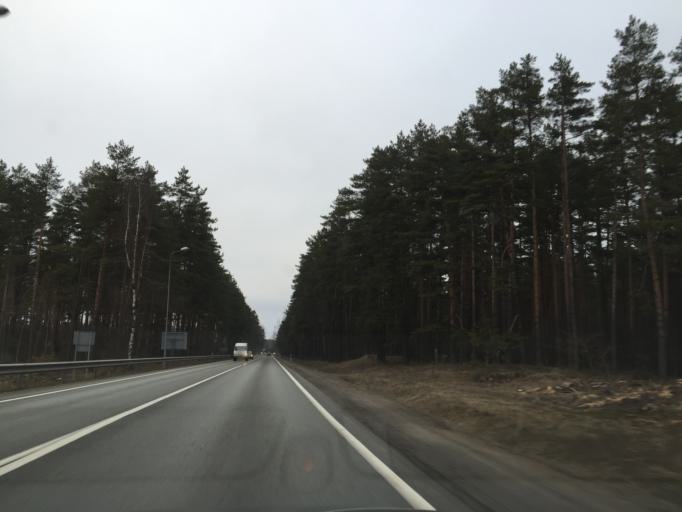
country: LV
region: Salaspils
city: Salaspils
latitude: 56.9439
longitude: 24.3819
